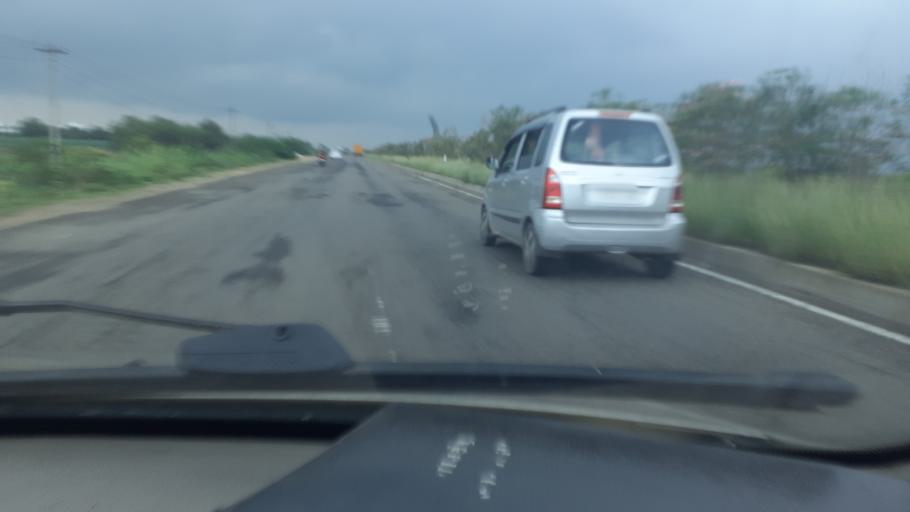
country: IN
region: Tamil Nadu
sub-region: Thoothukkudi
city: Kovilpatti
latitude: 9.1244
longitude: 77.8202
